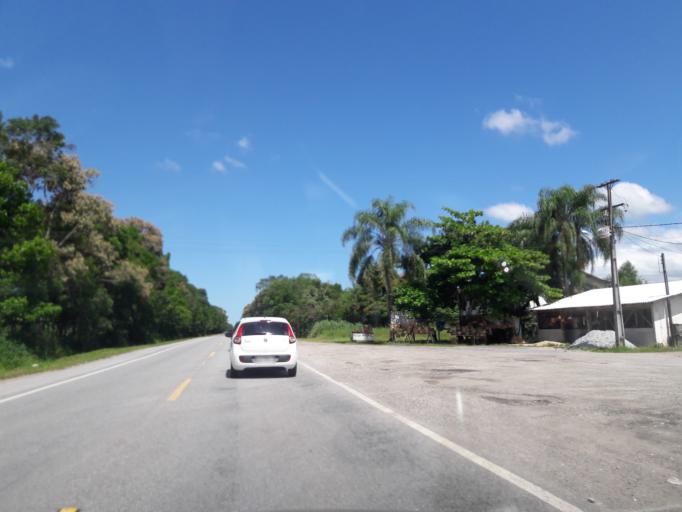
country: BR
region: Parana
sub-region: Pontal Do Parana
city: Pontal do Parana
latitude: -25.5992
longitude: -48.5589
